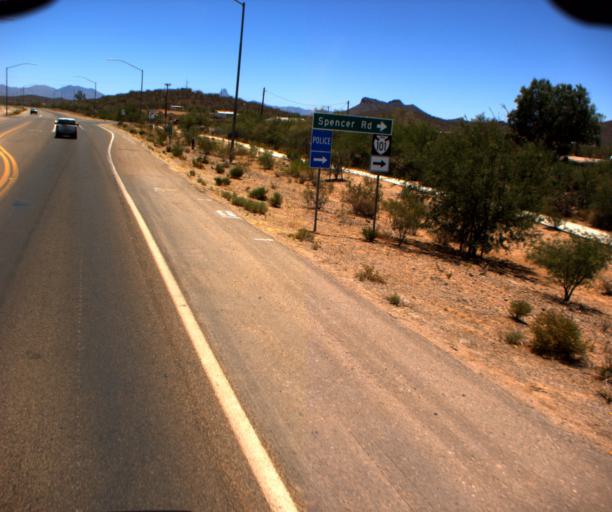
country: US
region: Arizona
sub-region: Pima County
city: Sells
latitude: 31.9189
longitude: -111.8816
